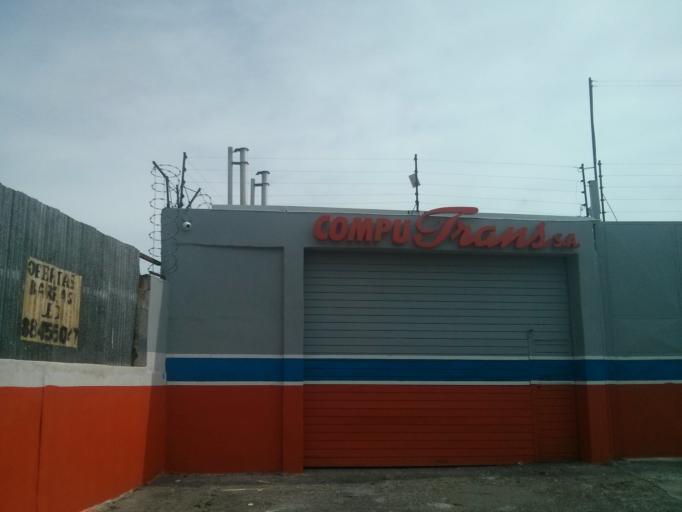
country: CR
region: San Jose
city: Colima
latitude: 9.9480
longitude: -84.0913
